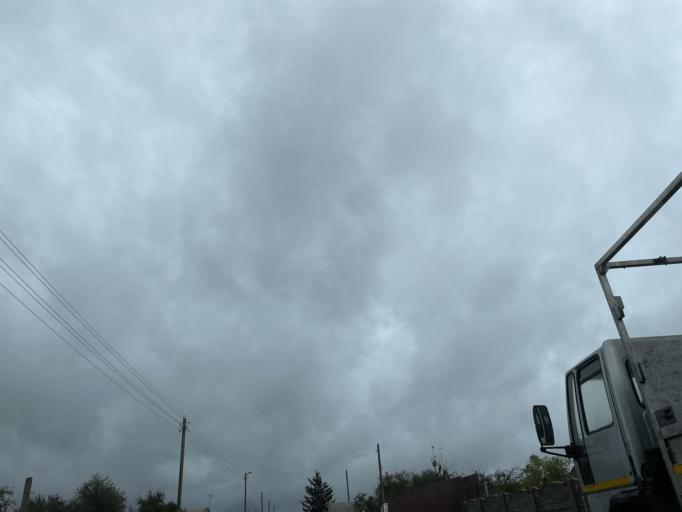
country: BY
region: Brest
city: Lyakhavichy
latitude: 53.1841
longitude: 26.2548
